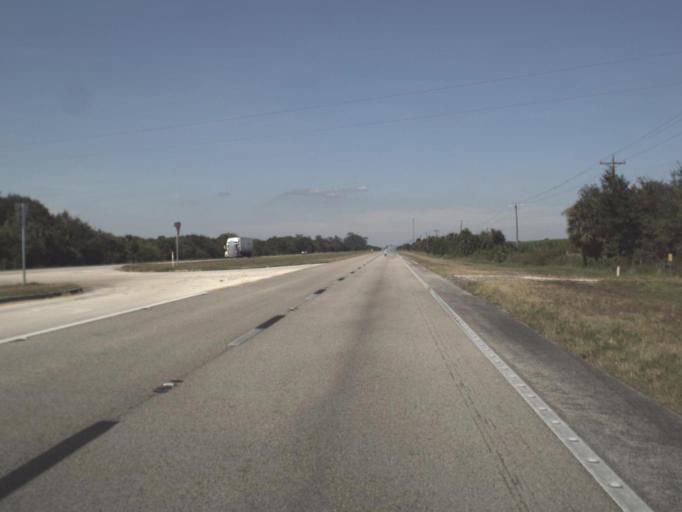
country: US
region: Florida
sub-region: Glades County
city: Moore Haven
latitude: 26.8488
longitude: -81.2022
